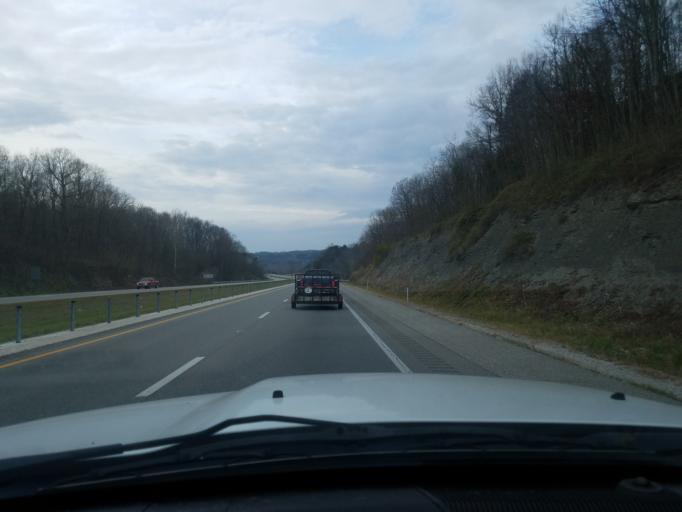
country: US
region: Kentucky
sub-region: Carter County
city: Olive Hill
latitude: 38.3249
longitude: -83.1057
